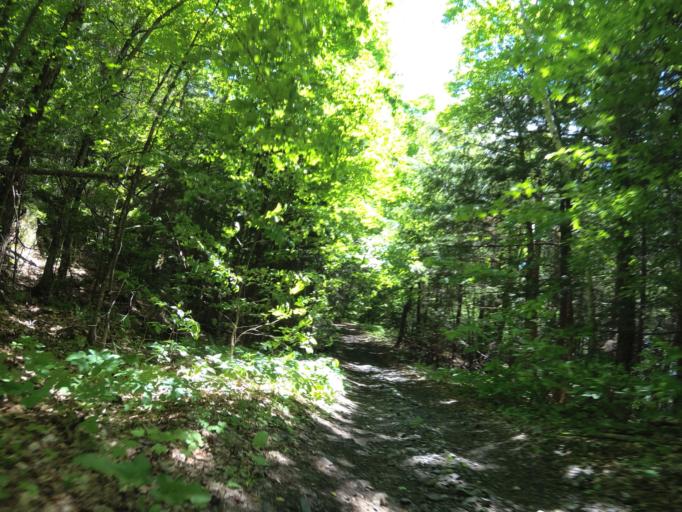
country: CA
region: Ontario
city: Renfrew
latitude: 45.0501
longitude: -76.8368
